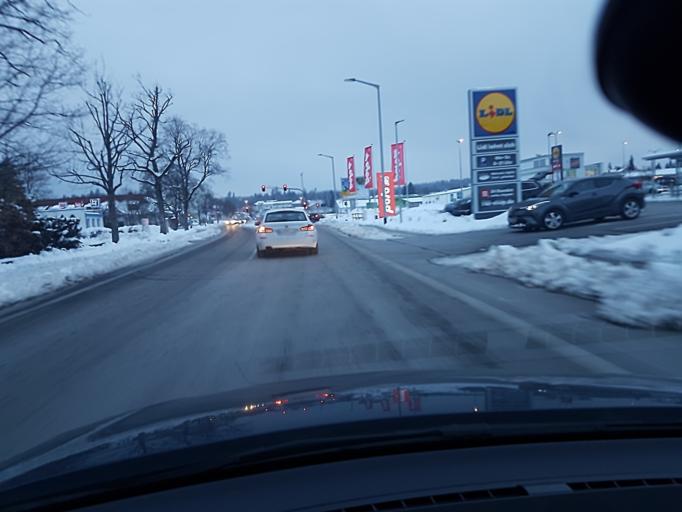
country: DE
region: Baden-Wuerttemberg
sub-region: Freiburg Region
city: Monchweiler
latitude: 48.0680
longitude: 8.4503
